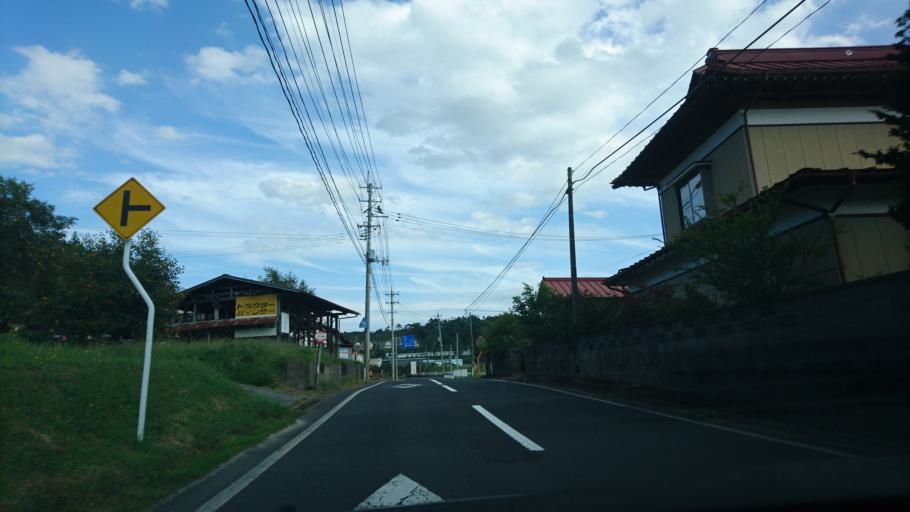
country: JP
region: Iwate
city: Ichinoseki
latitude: 38.8311
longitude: 141.2000
